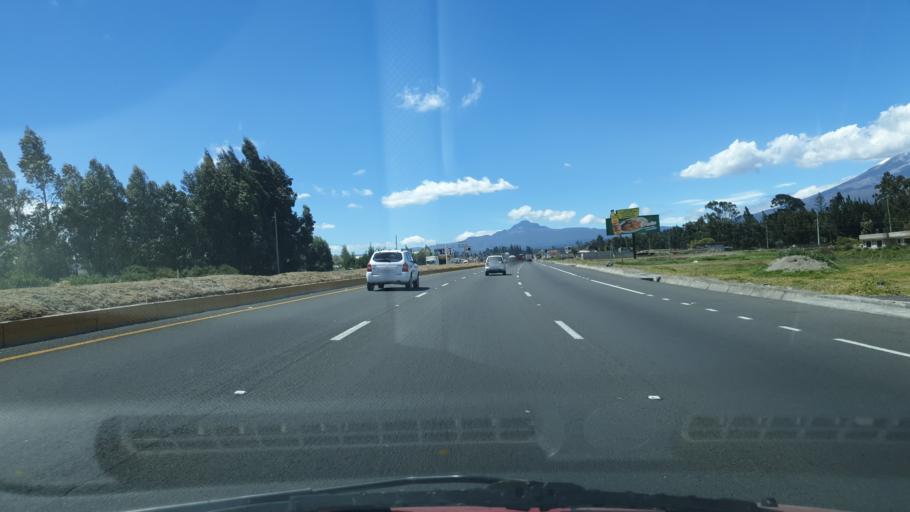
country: EC
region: Cotopaxi
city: Saquisili
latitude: -0.8118
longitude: -78.6248
